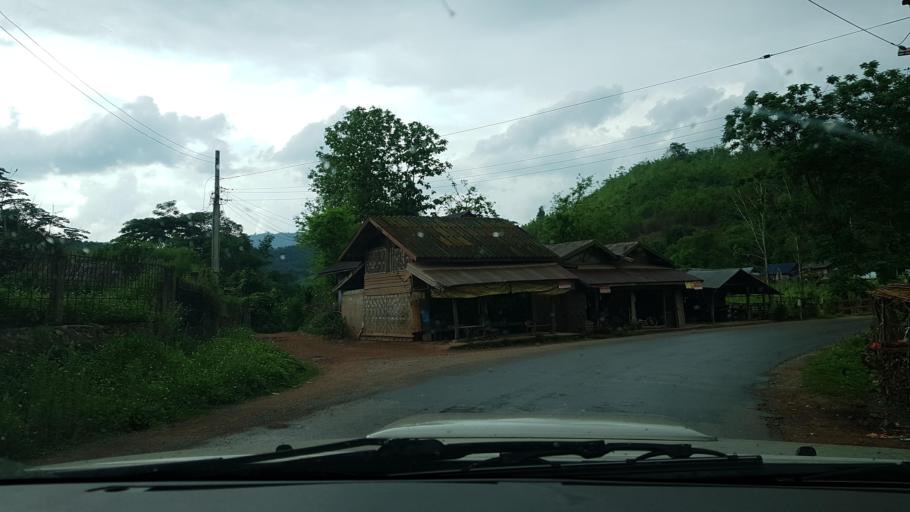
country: LA
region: Oudomxai
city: Muang Xay
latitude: 20.5812
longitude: 101.9202
